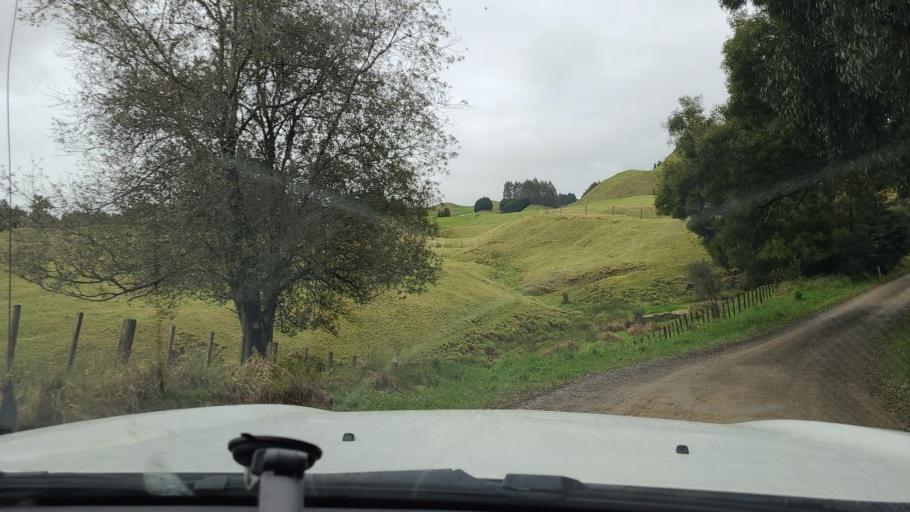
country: NZ
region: Hawke's Bay
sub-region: Wairoa District
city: Wairoa
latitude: -38.5603
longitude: 177.4881
